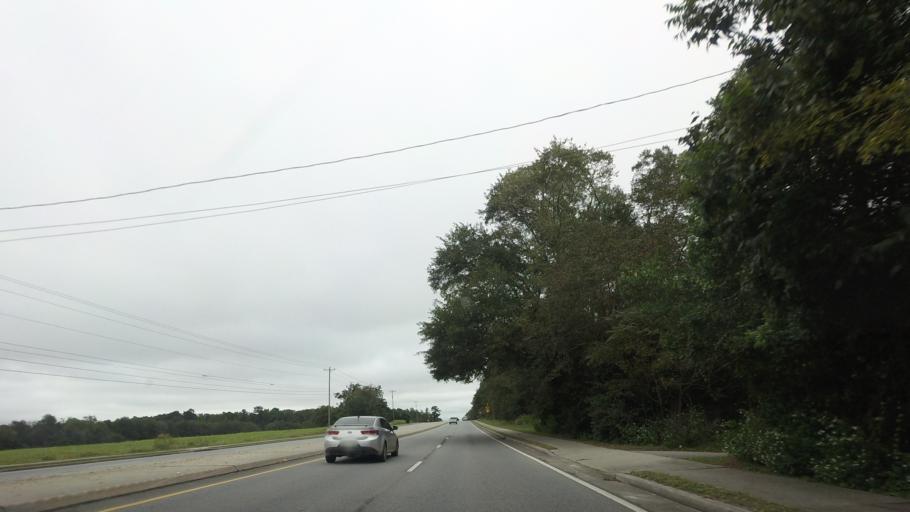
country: US
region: Georgia
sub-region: Lowndes County
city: Valdosta
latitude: 30.8993
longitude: -83.2672
